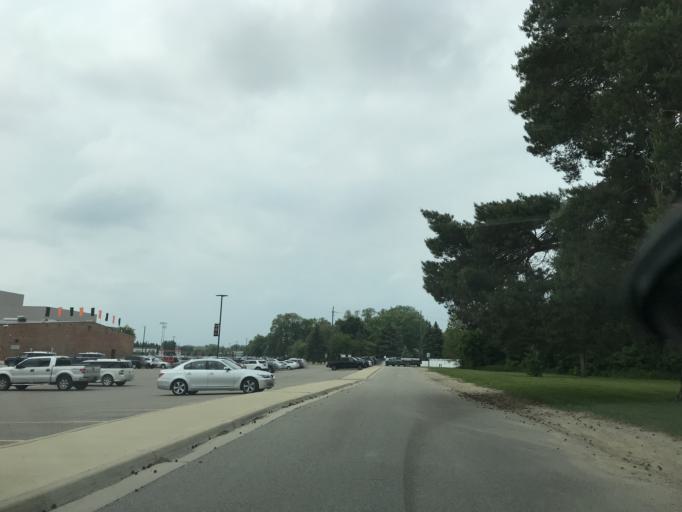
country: US
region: Michigan
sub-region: Livingston County
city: Brighton
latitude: 42.5269
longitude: -83.7930
